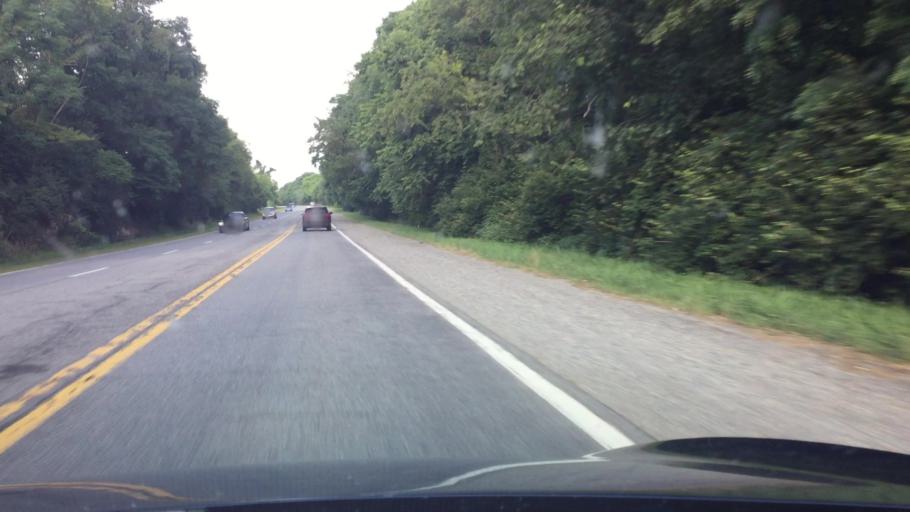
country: US
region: Virginia
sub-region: Pulaski County
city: Dublin
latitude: 37.1283
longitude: -80.6446
